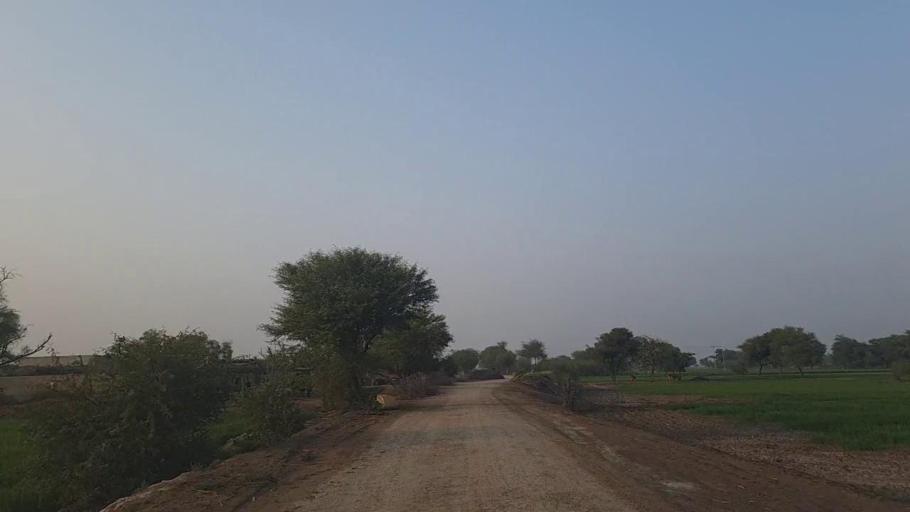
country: PK
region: Sindh
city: Nawabshah
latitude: 26.2523
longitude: 68.4723
